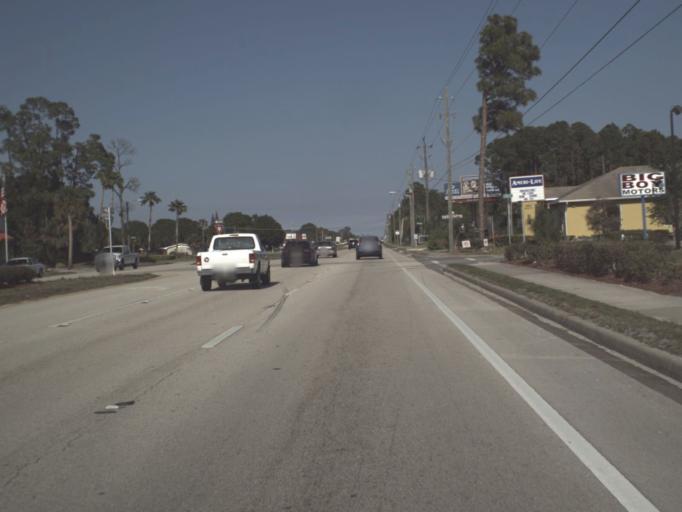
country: US
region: Florida
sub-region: Brevard County
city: June Park
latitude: 28.0788
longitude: -80.6913
